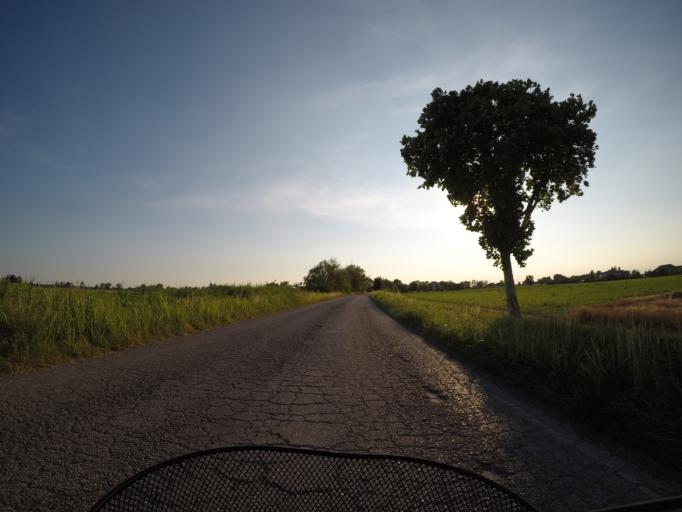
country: IT
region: Veneto
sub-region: Provincia di Rovigo
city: Fratta Polesine
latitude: 45.0284
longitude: 11.6314
